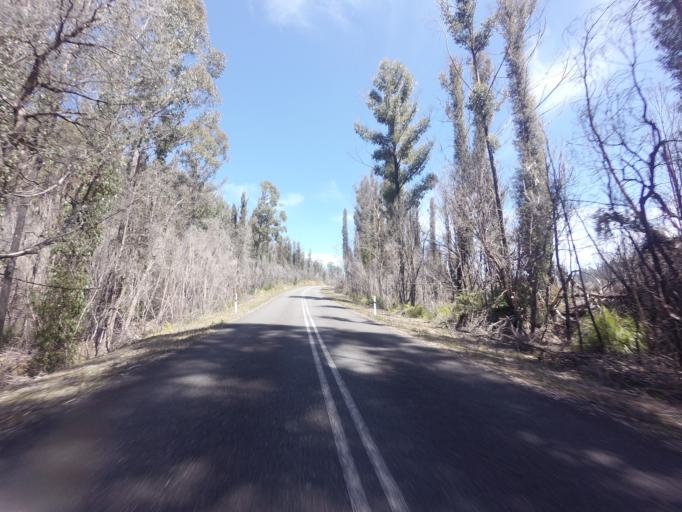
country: AU
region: Tasmania
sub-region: Huon Valley
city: Geeveston
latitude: -42.8381
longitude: 146.2624
